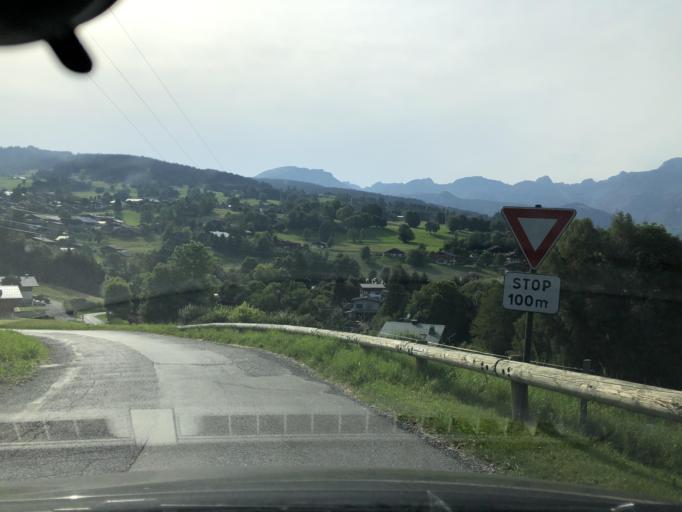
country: FR
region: Rhone-Alpes
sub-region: Departement de la Haute-Savoie
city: Combloux
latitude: 45.8847
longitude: 6.6485
